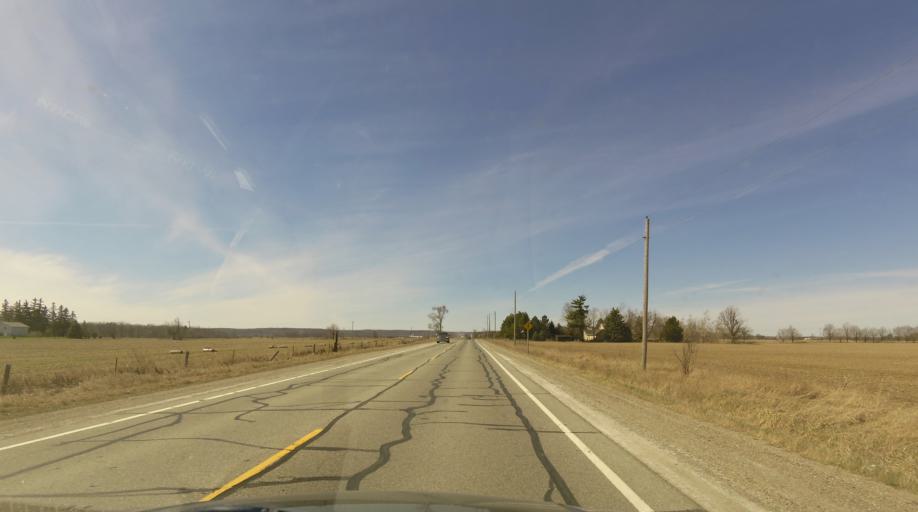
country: CA
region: Ontario
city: Brampton
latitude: 43.7127
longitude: -79.8917
